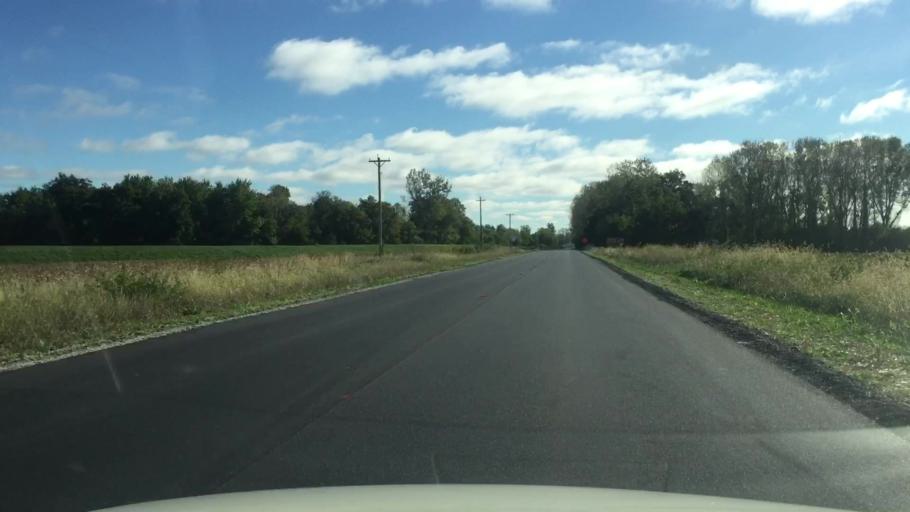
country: US
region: Missouri
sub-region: Howard County
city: New Franklin
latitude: 39.0033
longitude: -92.7194
